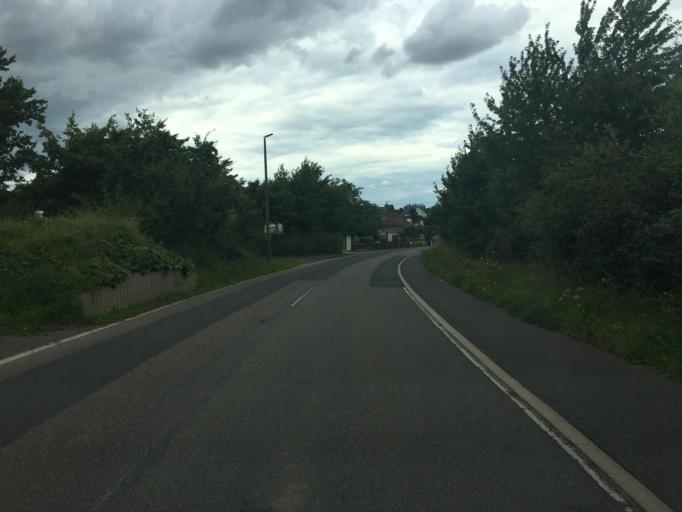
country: DE
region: North Rhine-Westphalia
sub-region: Regierungsbezirk Koln
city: Mechernich
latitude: 50.6068
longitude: 6.6592
